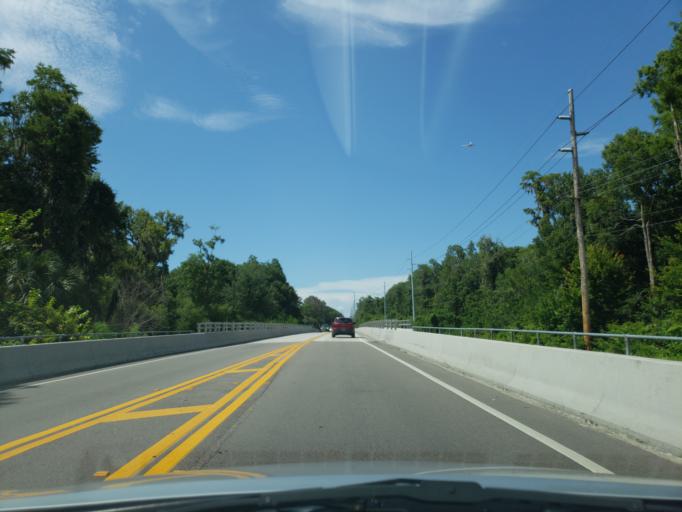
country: US
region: Florida
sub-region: Hillsborough County
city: Carrollwood Village
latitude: 28.0697
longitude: -82.5416
